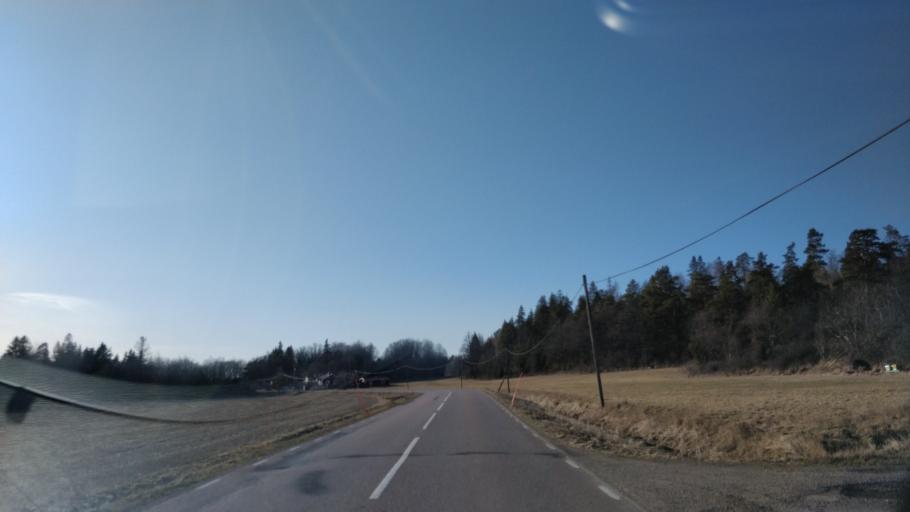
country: SE
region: Uppsala
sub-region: Enkopings Kommun
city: Orsundsbro
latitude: 59.7424
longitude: 17.2879
